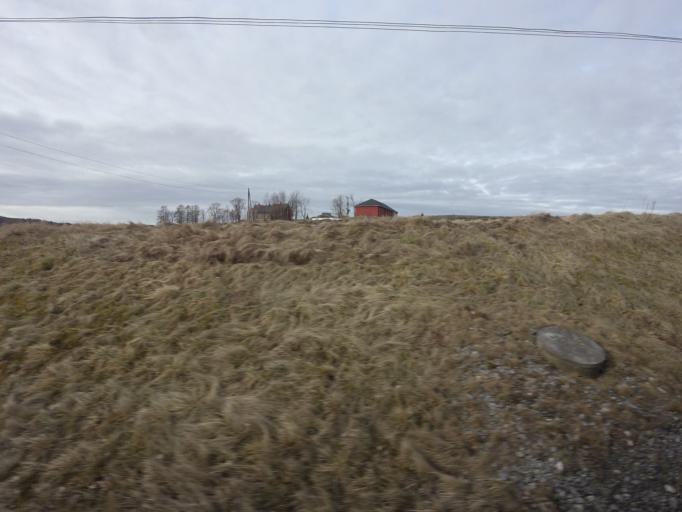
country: NO
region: Akershus
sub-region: Enebakk
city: Flateby
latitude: 59.8658
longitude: 11.2239
